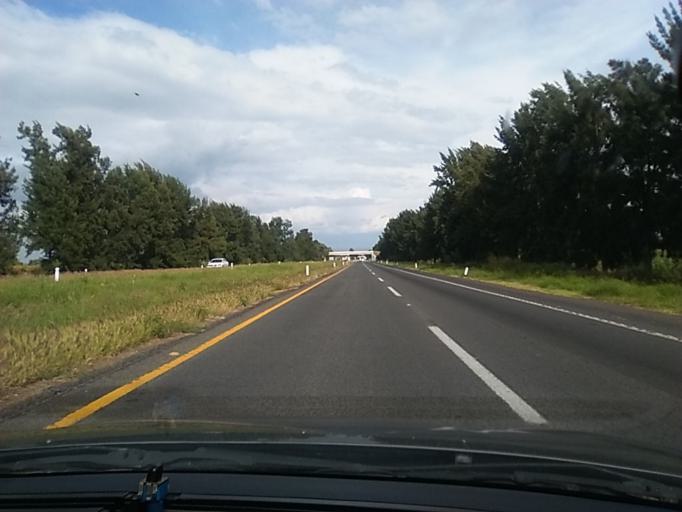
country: MX
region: Jalisco
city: La Barca
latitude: 20.3220
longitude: -102.5202
